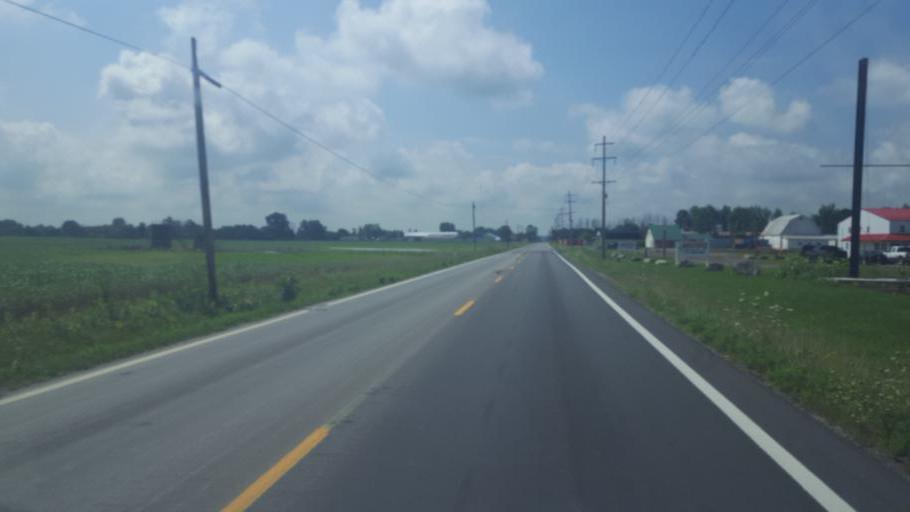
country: US
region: Ohio
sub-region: Fairfield County
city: Baltimore
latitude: 39.8513
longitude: -82.5677
